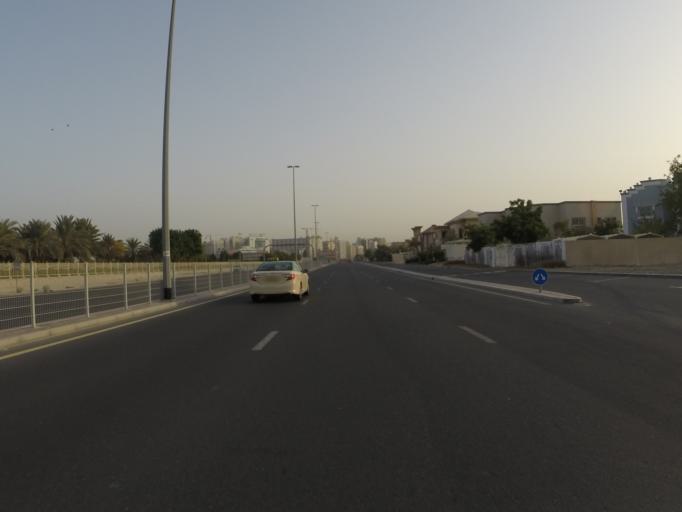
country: AE
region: Dubai
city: Dubai
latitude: 25.1010
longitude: 55.2062
